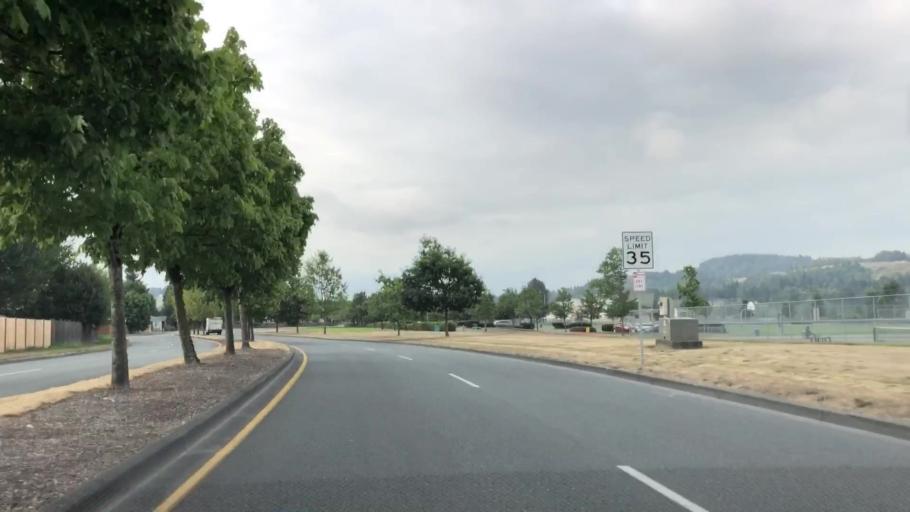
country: US
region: Washington
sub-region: Snohomish County
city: Monroe
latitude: 47.8620
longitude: -122.0098
